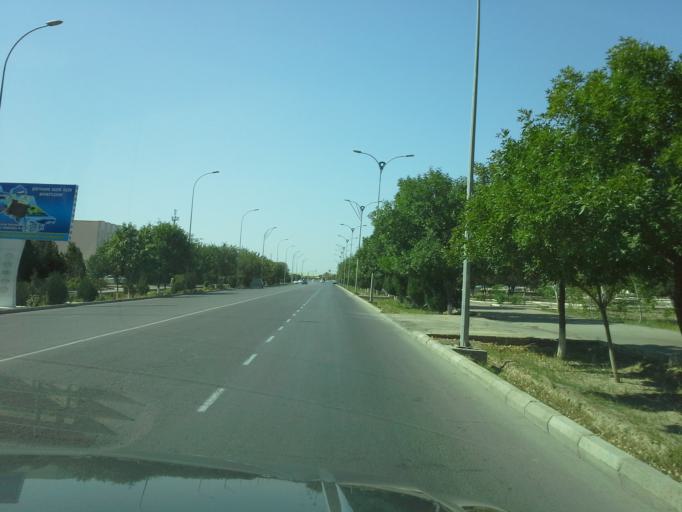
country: TM
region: Dasoguz
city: Dasoguz
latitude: 41.8437
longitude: 59.9358
